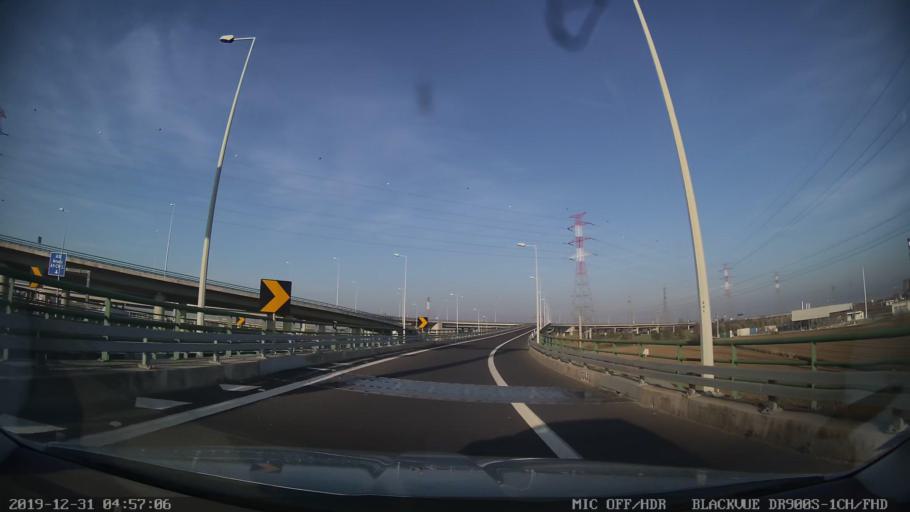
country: PT
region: Lisbon
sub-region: Alenquer
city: Carregado
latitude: 39.0150
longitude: -8.9656
